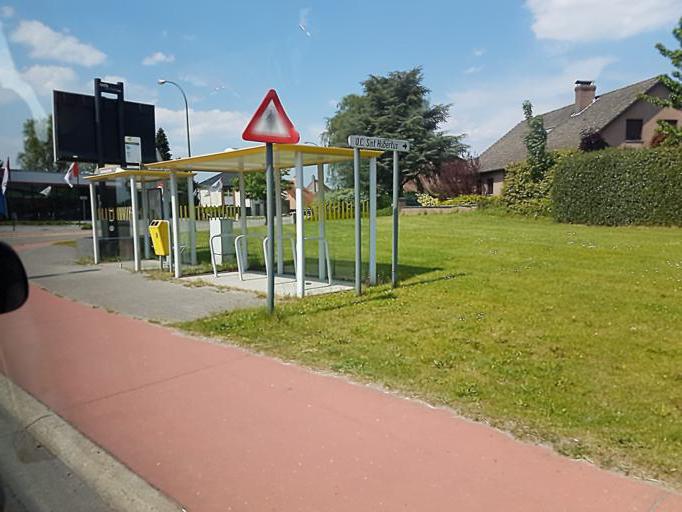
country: BE
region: Flanders
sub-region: Provincie Limburg
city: Neerpelt
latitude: 51.2207
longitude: 5.4827
